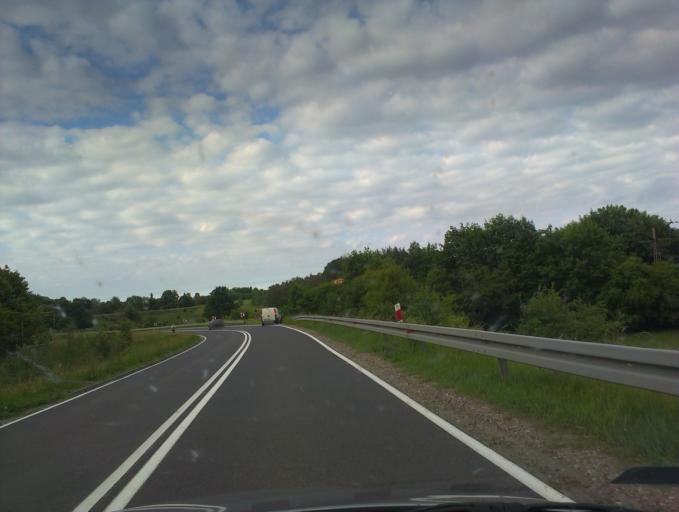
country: PL
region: West Pomeranian Voivodeship
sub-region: Powiat szczecinecki
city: Szczecinek
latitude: 53.6811
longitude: 16.6876
